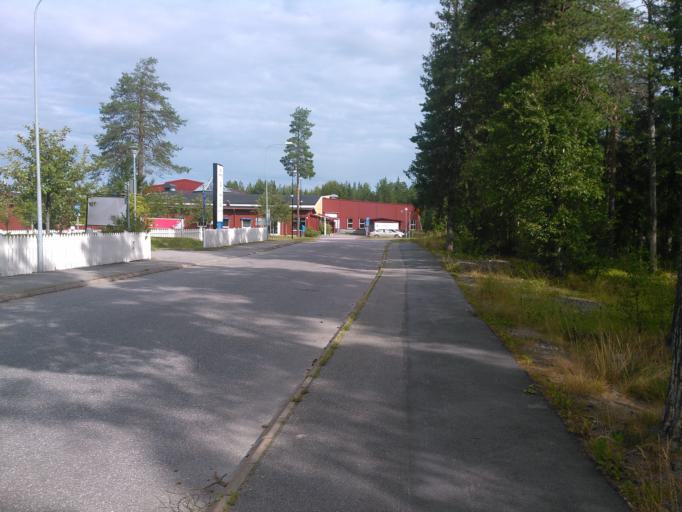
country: SE
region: Vaesterbotten
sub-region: Umea Kommun
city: Umea
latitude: 63.8173
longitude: 20.3211
